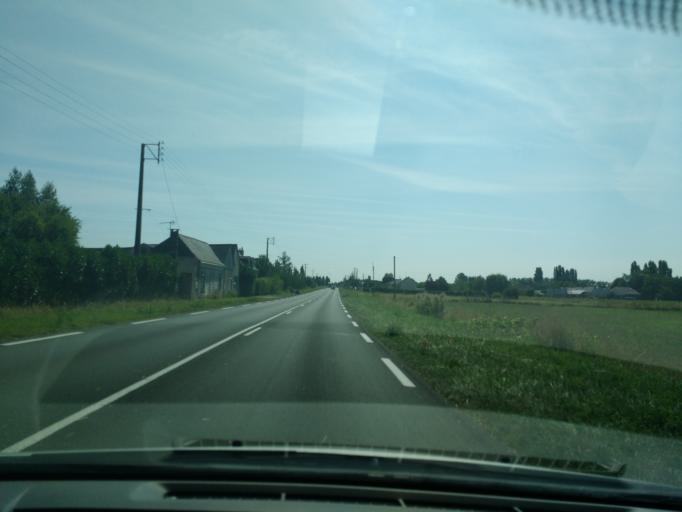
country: FR
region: Pays de la Loire
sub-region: Departement de Maine-et-Loire
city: Maze
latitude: 47.4651
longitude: -0.2935
